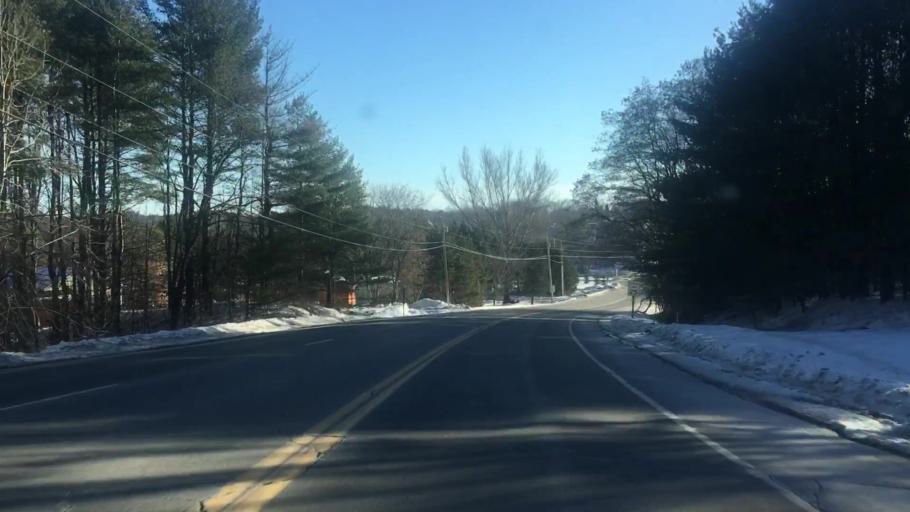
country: US
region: Maine
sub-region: Somerset County
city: Norridgewock
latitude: 44.7200
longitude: -69.7980
